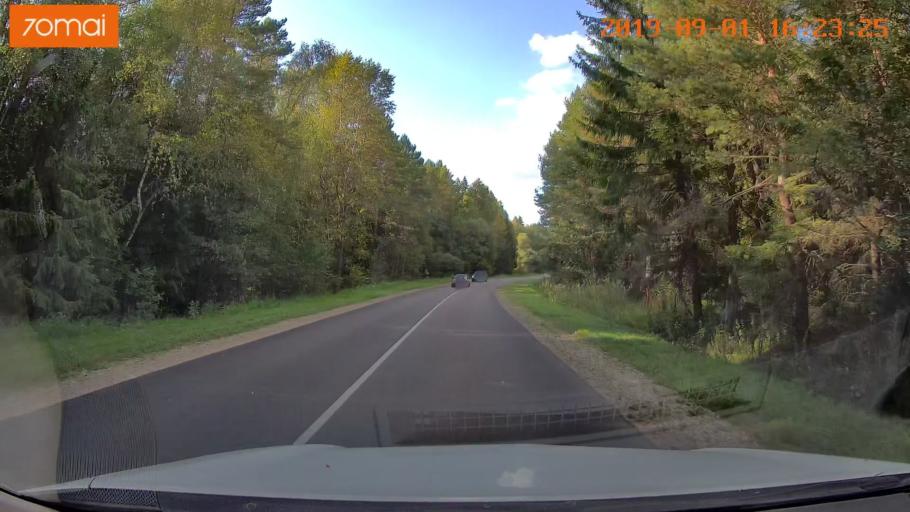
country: RU
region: Kaluga
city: Maloyaroslavets
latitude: 54.8810
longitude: 36.5330
